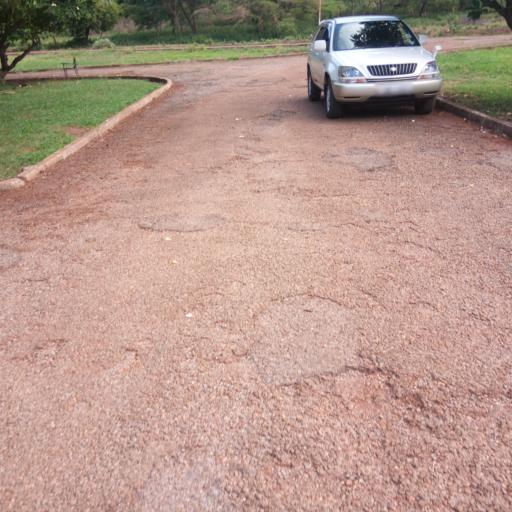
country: UG
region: Eastern Region
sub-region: Busia District
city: Busia
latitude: 0.5448
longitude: 34.0199
